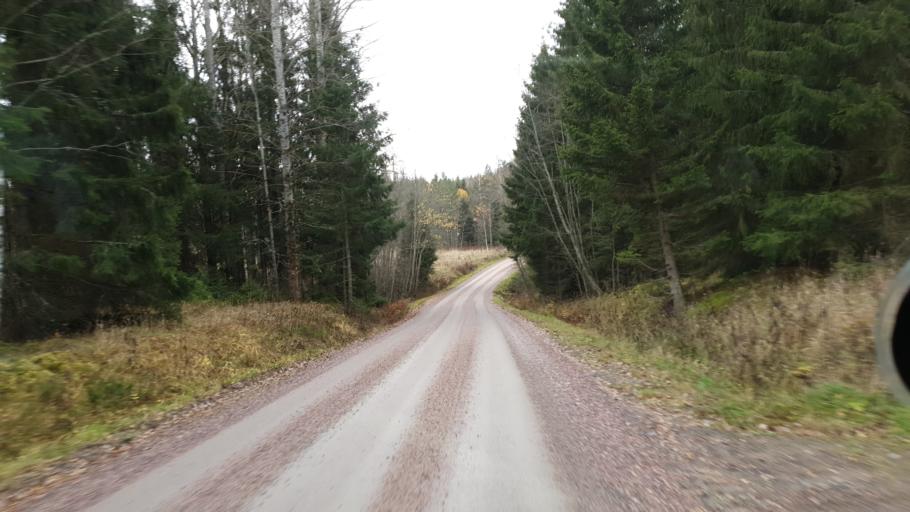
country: FI
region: Uusimaa
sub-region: Helsinki
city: Siuntio
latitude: 60.1474
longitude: 24.2712
